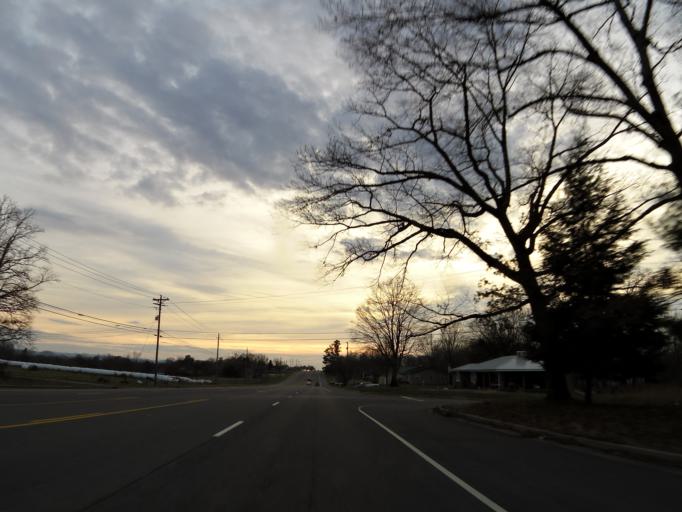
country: US
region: Tennessee
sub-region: Monroe County
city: Madisonville
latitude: 35.4890
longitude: -84.3964
